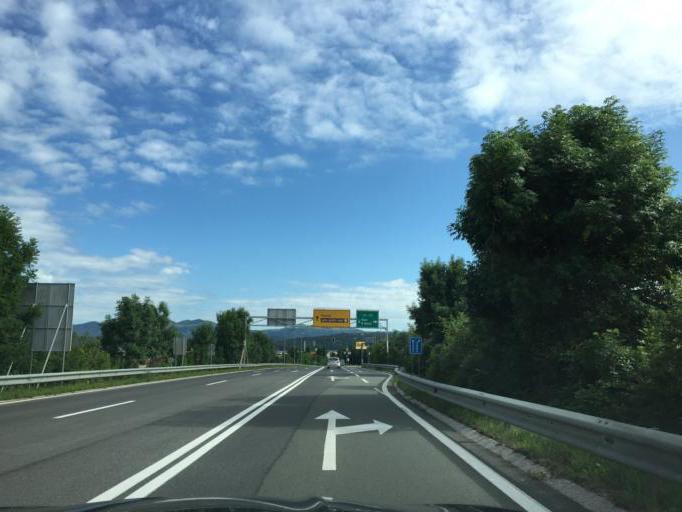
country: SI
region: Postojna
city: Postojna
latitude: 45.7607
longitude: 14.1954
